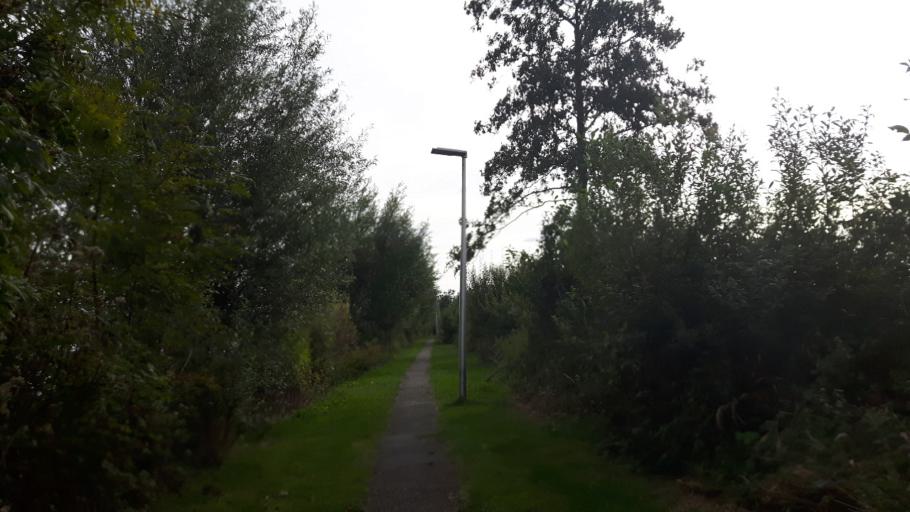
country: NL
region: Utrecht
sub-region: Gemeente De Ronde Venen
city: Mijdrecht
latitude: 52.1680
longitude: 4.8378
